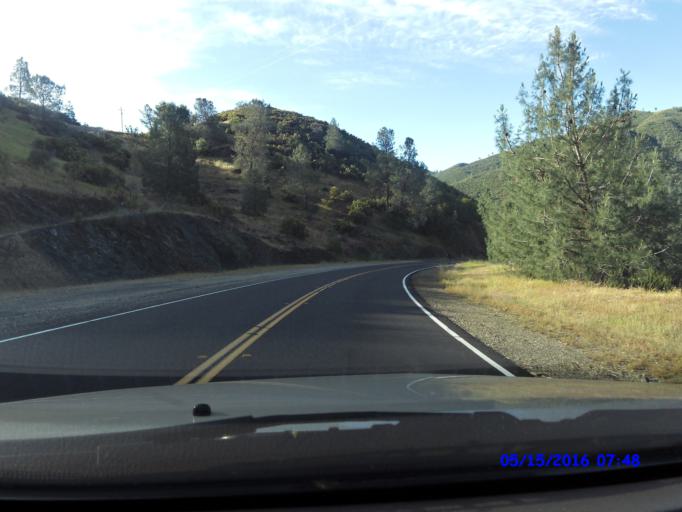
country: US
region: California
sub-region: Mariposa County
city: Mariposa
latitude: 37.6194
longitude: -120.1414
